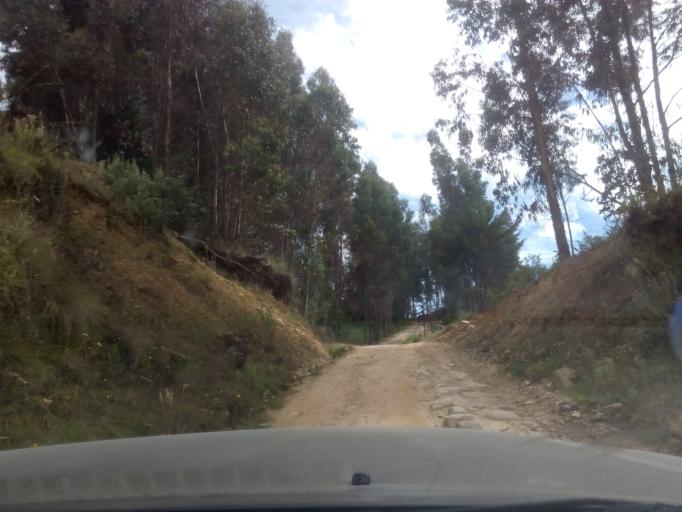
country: PE
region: La Libertad
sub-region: Sanchez Carrion
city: Curgos
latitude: -7.8637
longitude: -77.9726
